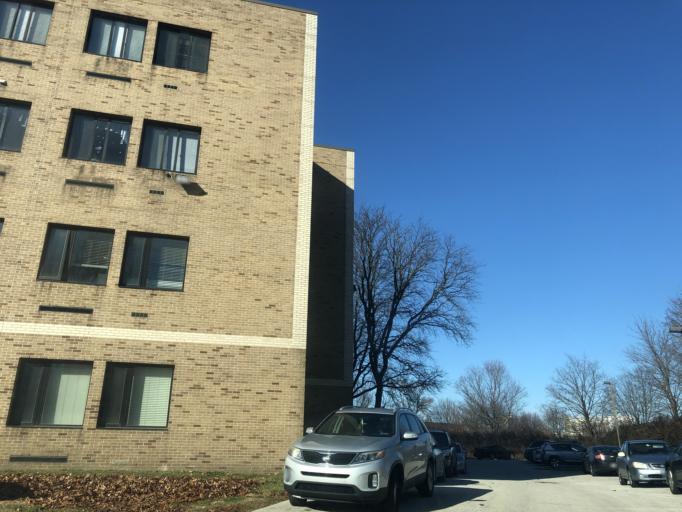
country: US
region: Pennsylvania
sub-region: Montgomery County
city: Bala-Cynwyd
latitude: 39.9966
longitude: -75.2155
